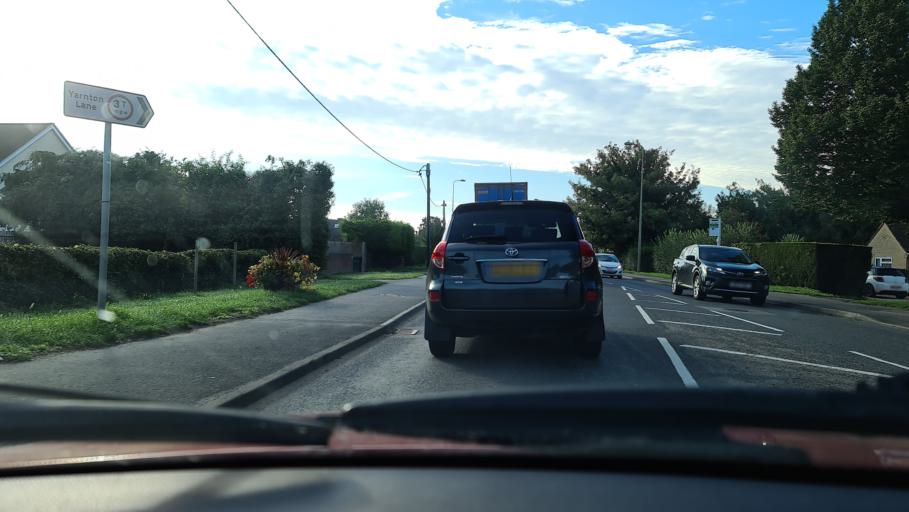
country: GB
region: England
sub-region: Oxfordshire
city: Kidlington
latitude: 51.8211
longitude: -1.2877
